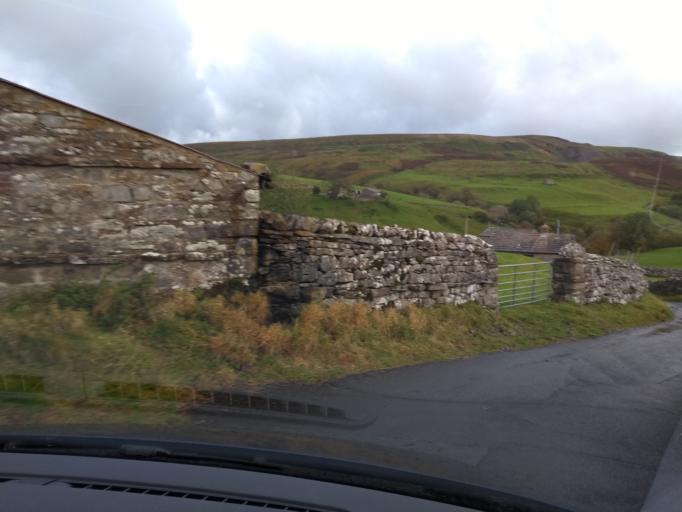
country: GB
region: England
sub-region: County Durham
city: Bowes
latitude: 54.4049
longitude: -2.1682
